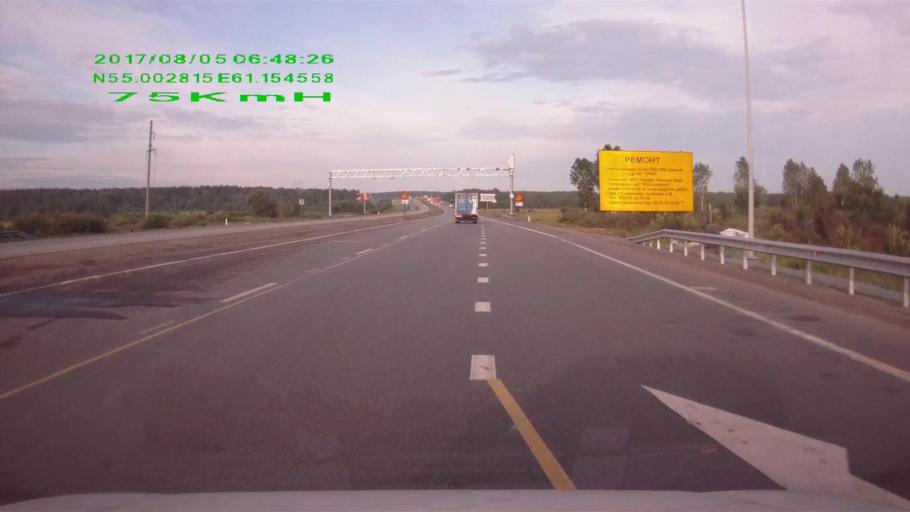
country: RU
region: Chelyabinsk
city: Poletayevo
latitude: 55.0028
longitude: 61.1545
